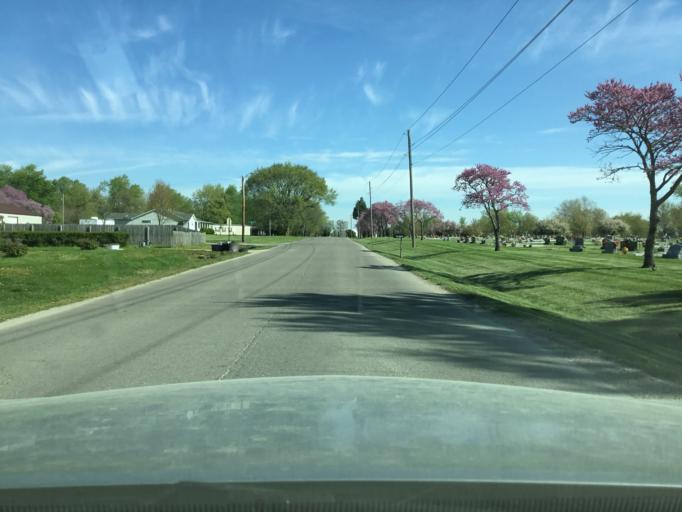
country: US
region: Kansas
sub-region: Neosho County
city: Chanute
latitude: 37.6633
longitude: -95.4434
